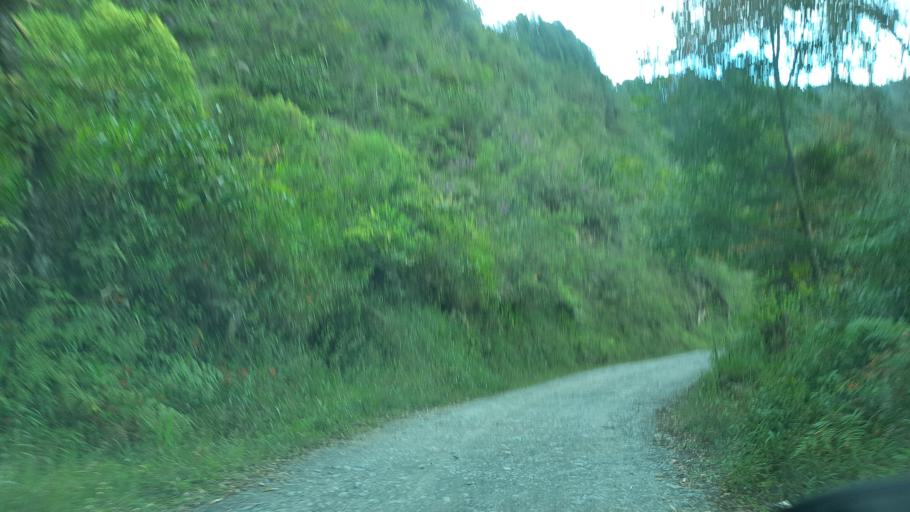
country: CO
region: Boyaca
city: Garagoa
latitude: 4.9869
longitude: -73.3294
